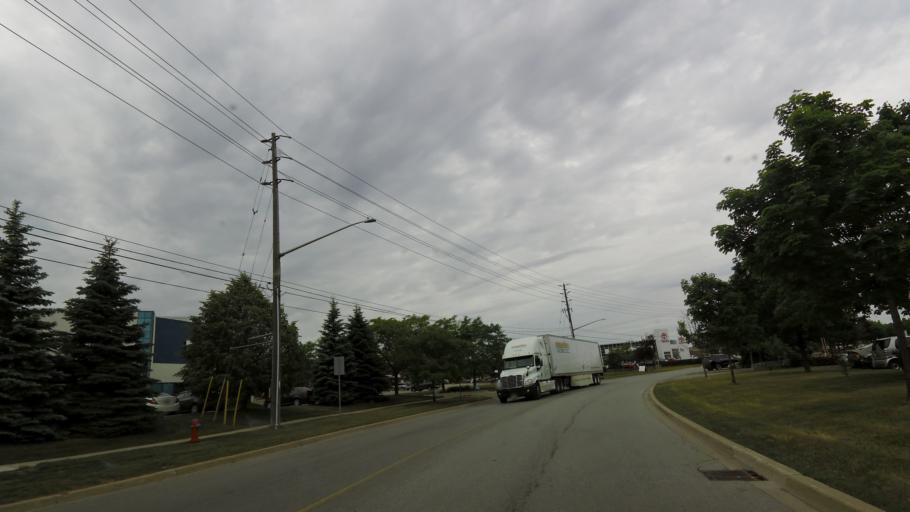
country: CA
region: Ontario
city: Oakville
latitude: 43.4105
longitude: -79.7330
